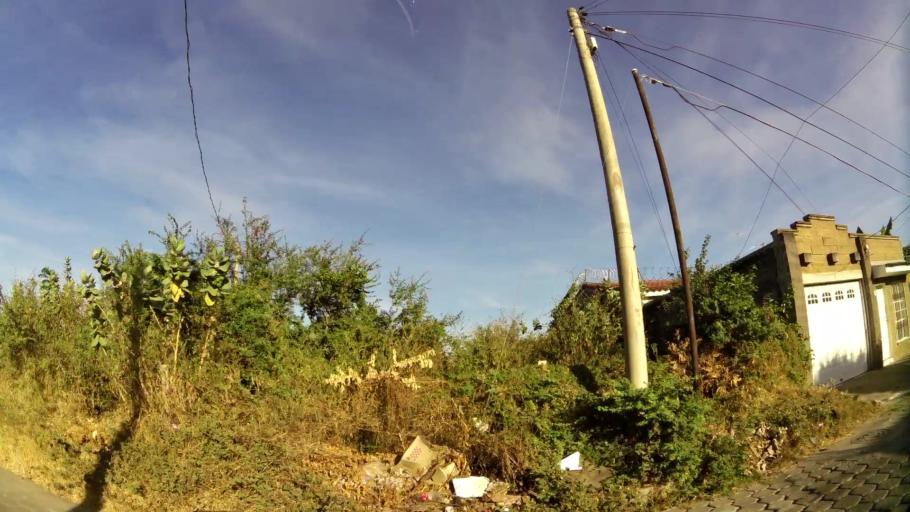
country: SV
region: San Miguel
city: San Miguel
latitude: 13.4570
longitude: -88.1671
